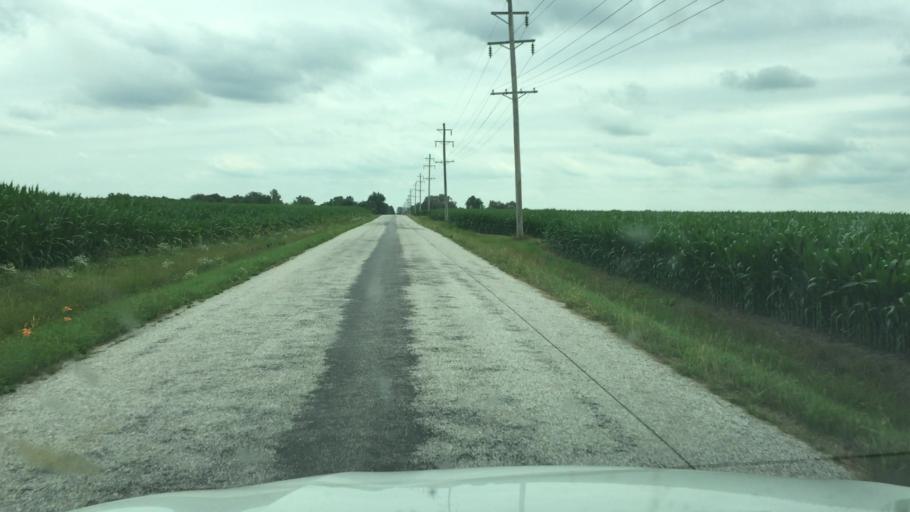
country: US
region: Illinois
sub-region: Hancock County
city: Carthage
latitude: 40.3372
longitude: -91.0824
